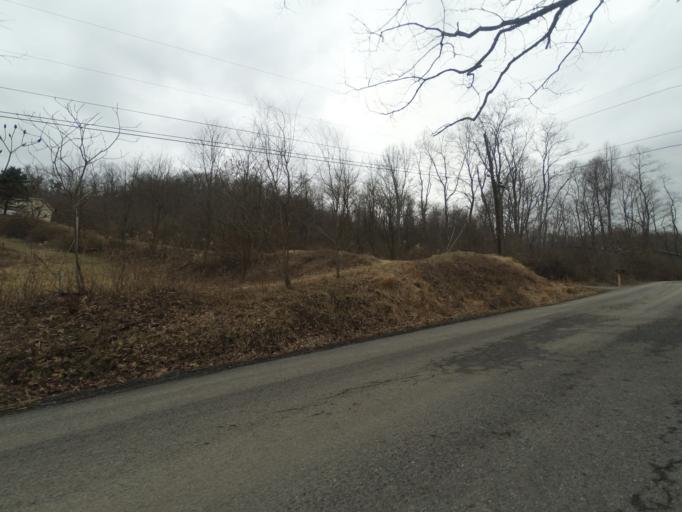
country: US
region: Pennsylvania
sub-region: Centre County
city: Stormstown
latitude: 40.8690
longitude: -78.0085
